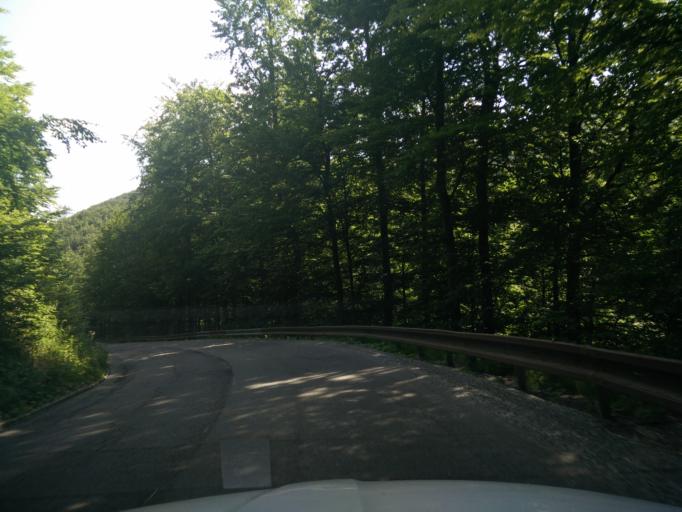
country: SK
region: Zilinsky
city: Rajec
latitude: 48.9527
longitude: 18.6226
